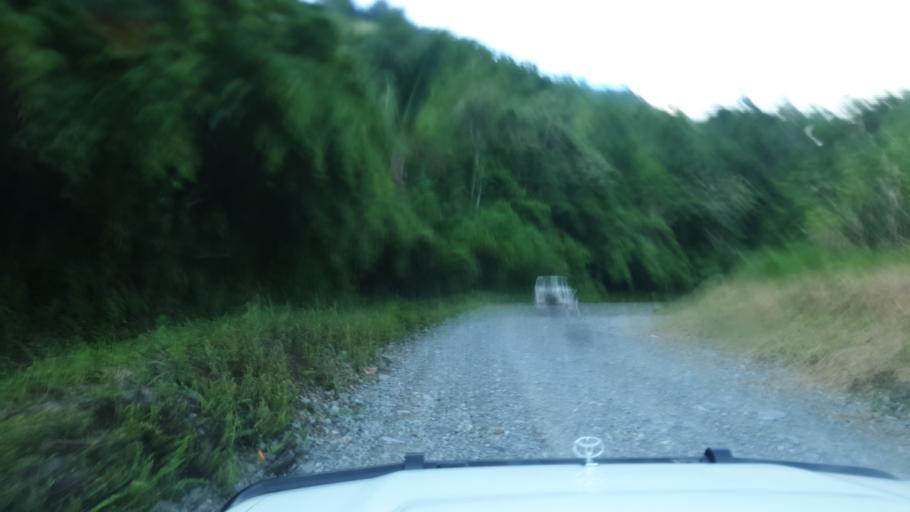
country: PG
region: Bougainville
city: Panguna
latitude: -6.3378
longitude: 155.4594
